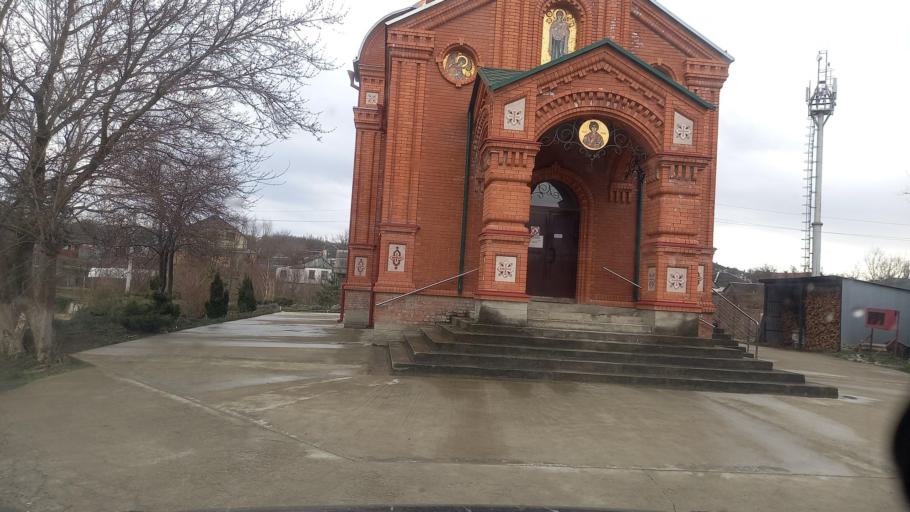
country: RU
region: Krasnodarskiy
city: Krymsk
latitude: 44.8654
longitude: 37.8585
